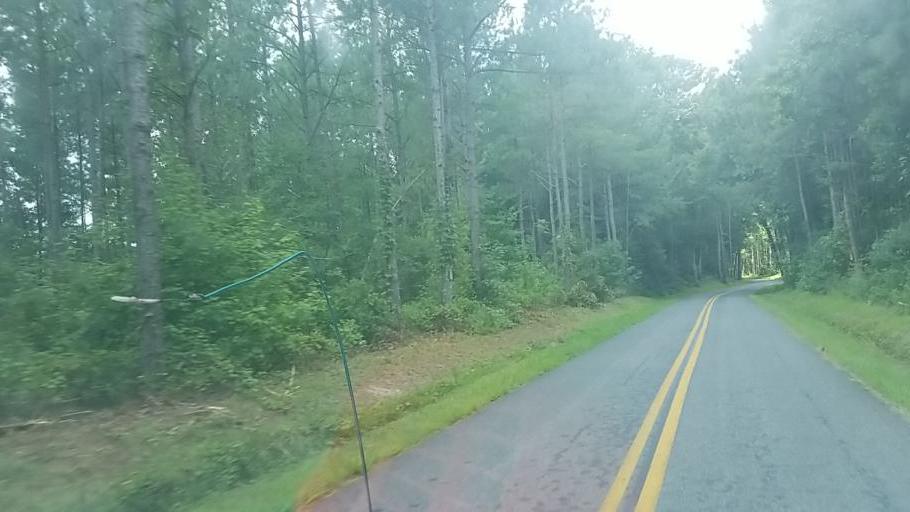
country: US
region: Maryland
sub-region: Worcester County
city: Snow Hill
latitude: 38.2619
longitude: -75.4563
